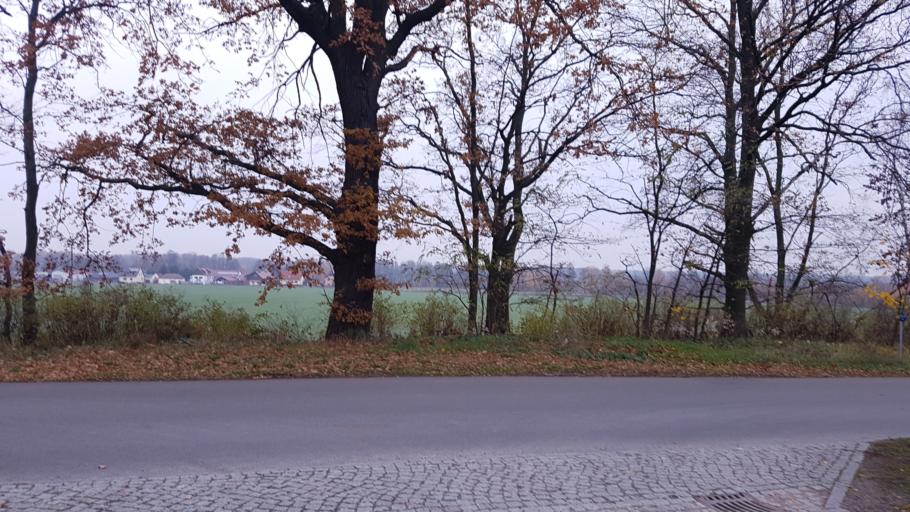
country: DE
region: Brandenburg
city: Grosskmehlen
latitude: 51.3743
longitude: 13.7332
